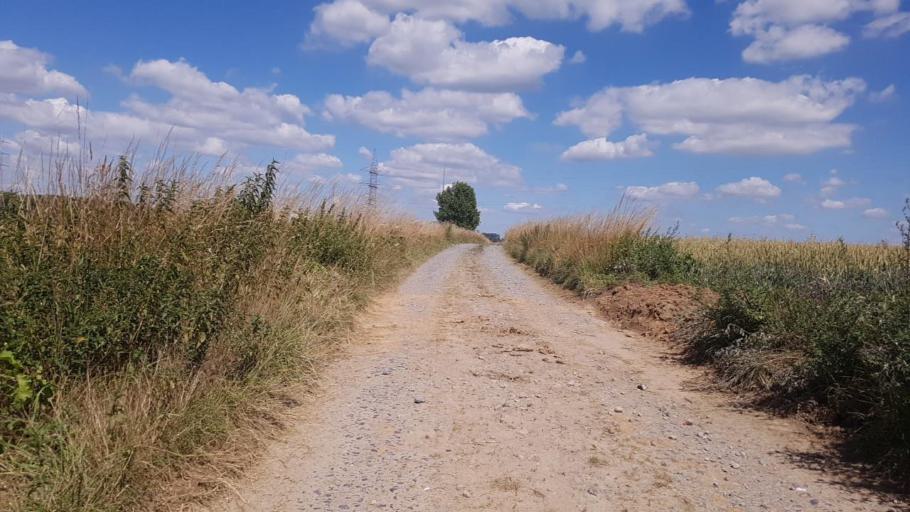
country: BE
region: Wallonia
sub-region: Province du Hainaut
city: Thuin
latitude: 50.3102
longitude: 4.3433
